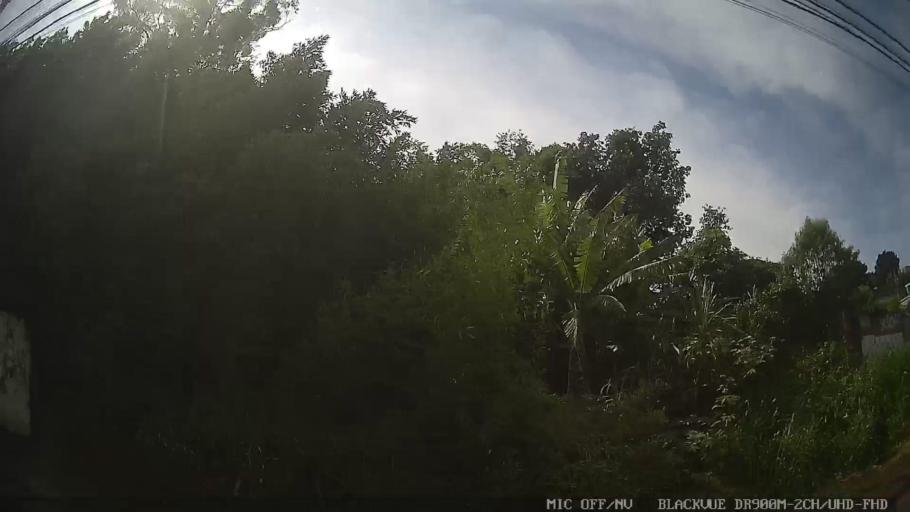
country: BR
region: Sao Paulo
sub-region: Itaquaquecetuba
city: Itaquaquecetuba
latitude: -23.4715
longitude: -46.3151
